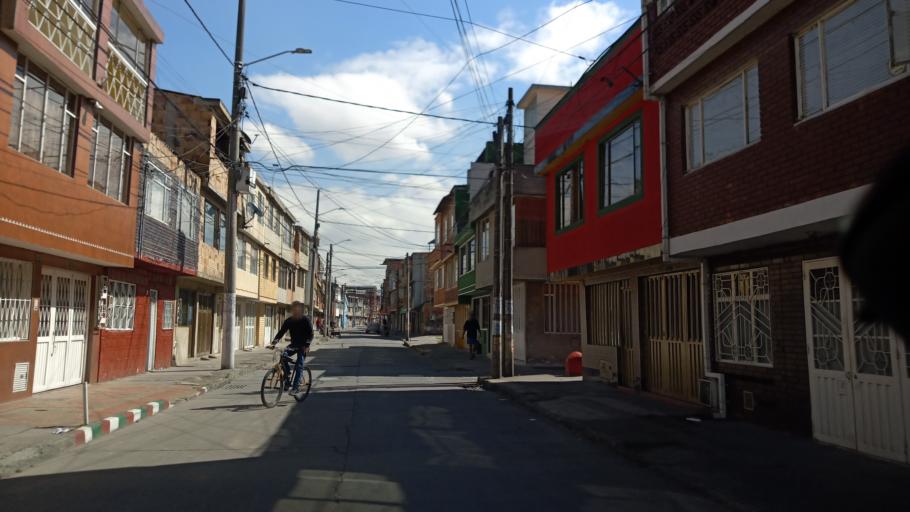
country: CO
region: Cundinamarca
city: Funza
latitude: 4.6712
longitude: -74.1507
